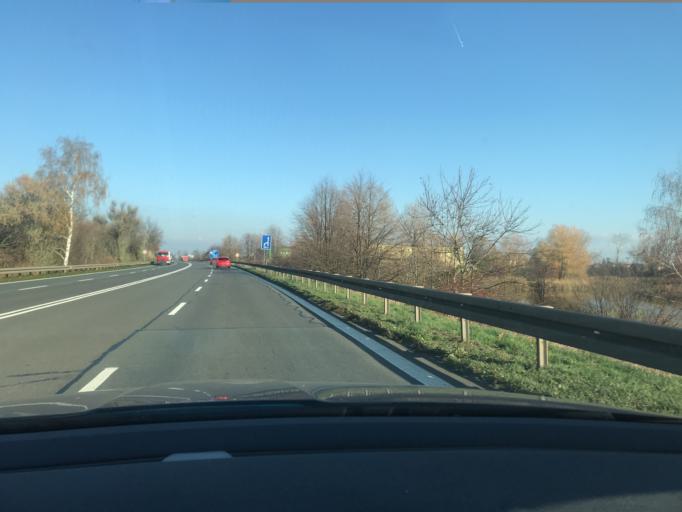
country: CZ
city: Stezery
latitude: 50.2167
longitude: 15.7871
